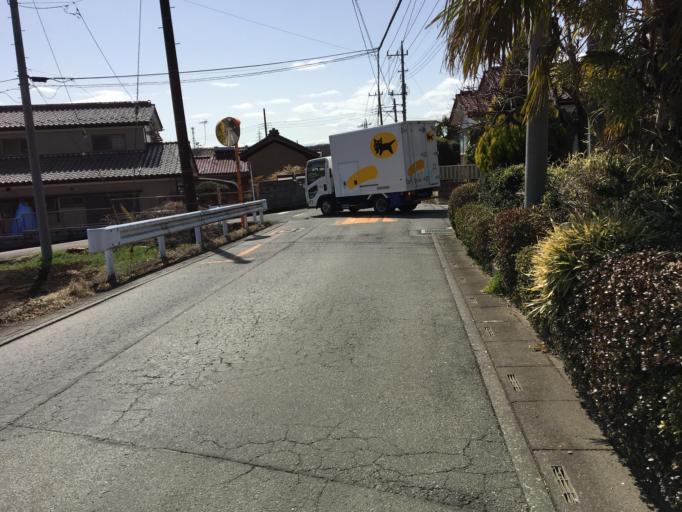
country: JP
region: Saitama
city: Ogawa
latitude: 36.0209
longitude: 139.3282
